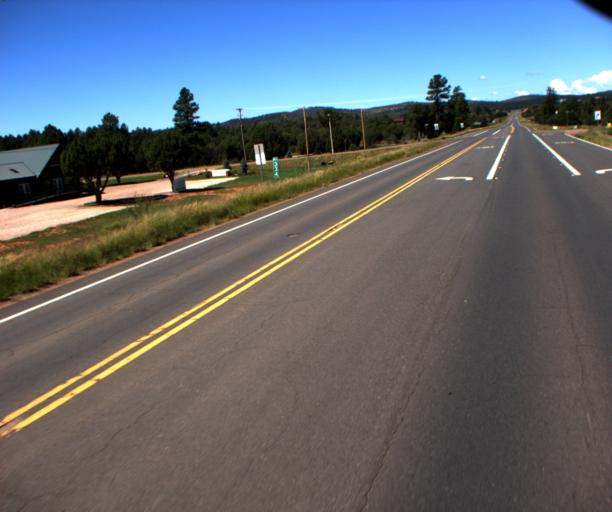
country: US
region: Arizona
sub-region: Navajo County
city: Linden
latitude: 34.2854
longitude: -110.1371
